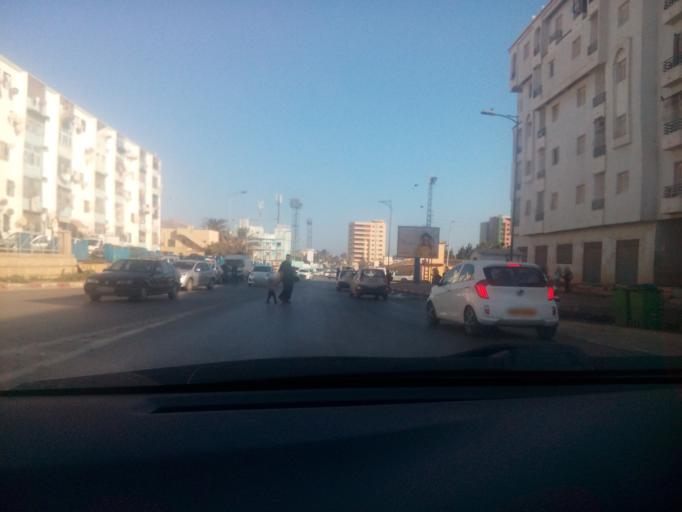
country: DZ
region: Oran
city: Oran
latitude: 35.6770
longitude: -0.6763
